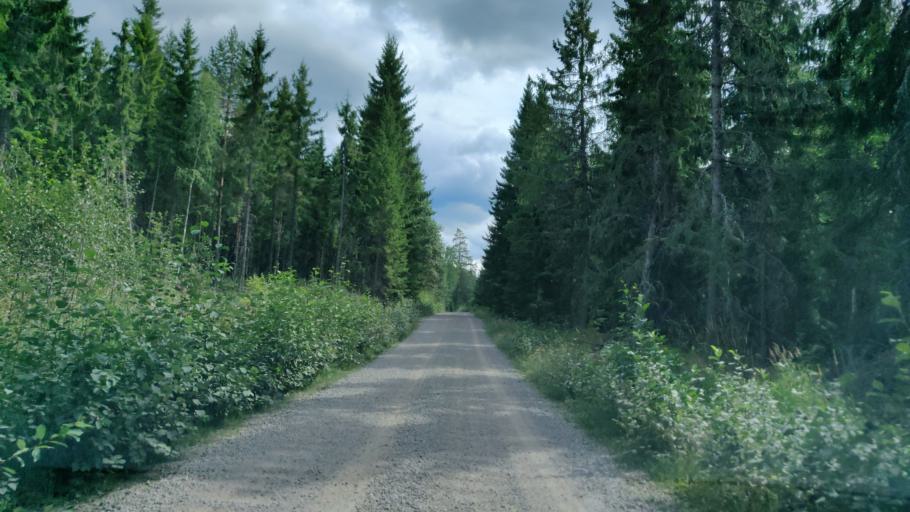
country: SE
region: Vaermland
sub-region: Hagfors Kommun
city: Hagfors
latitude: 60.0083
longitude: 13.7106
